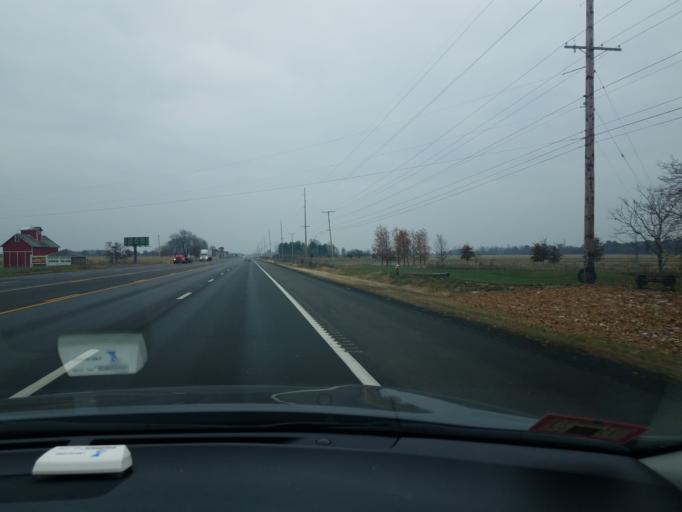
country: US
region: Ohio
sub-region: Erie County
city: Milan
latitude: 41.3735
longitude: -82.6422
